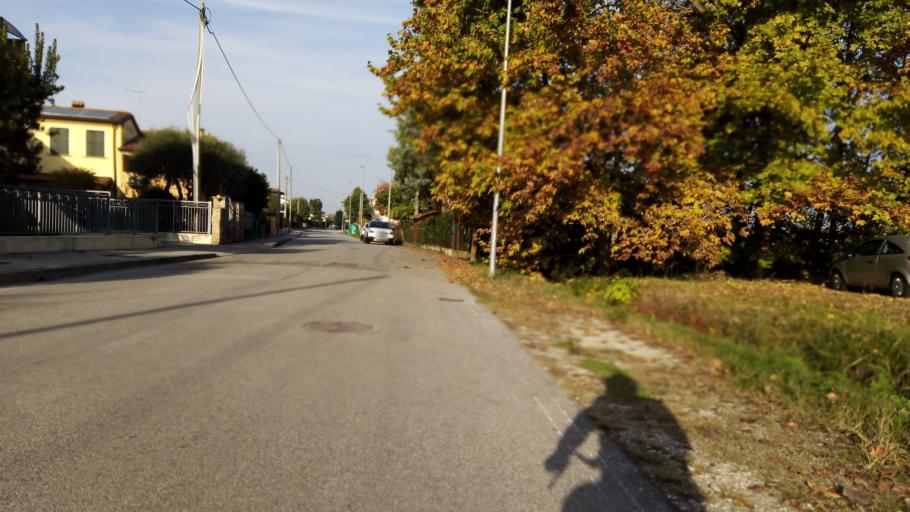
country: IT
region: Veneto
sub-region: Provincia di Padova
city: Abano Terme
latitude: 45.3655
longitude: 11.7963
